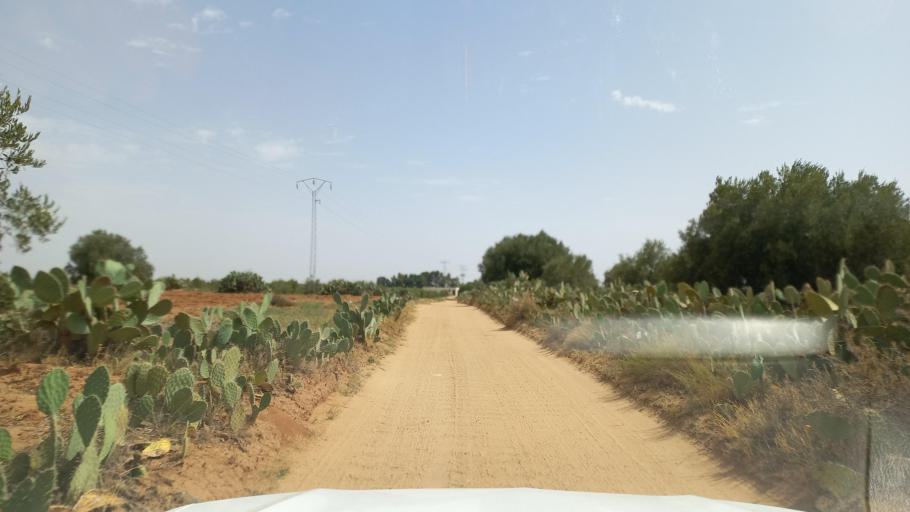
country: TN
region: Al Qasrayn
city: Kasserine
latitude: 35.2598
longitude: 9.0524
